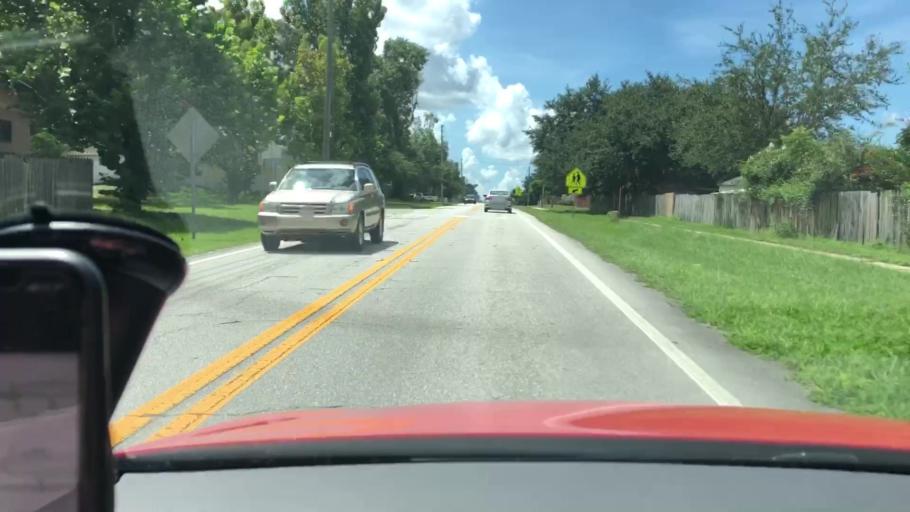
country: US
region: Florida
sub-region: Lake County
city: Eustis
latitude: 28.8513
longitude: -81.6547
